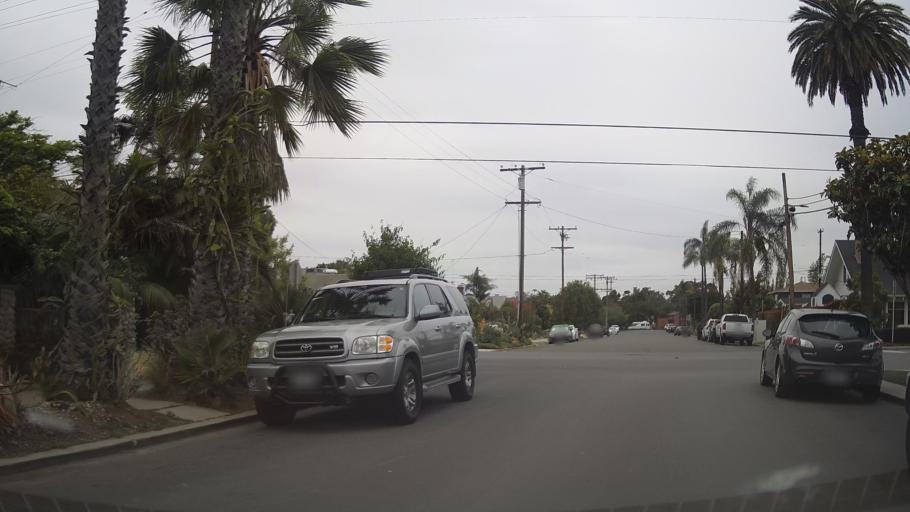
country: US
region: California
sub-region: San Diego County
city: San Diego
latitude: 32.7520
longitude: -117.1535
